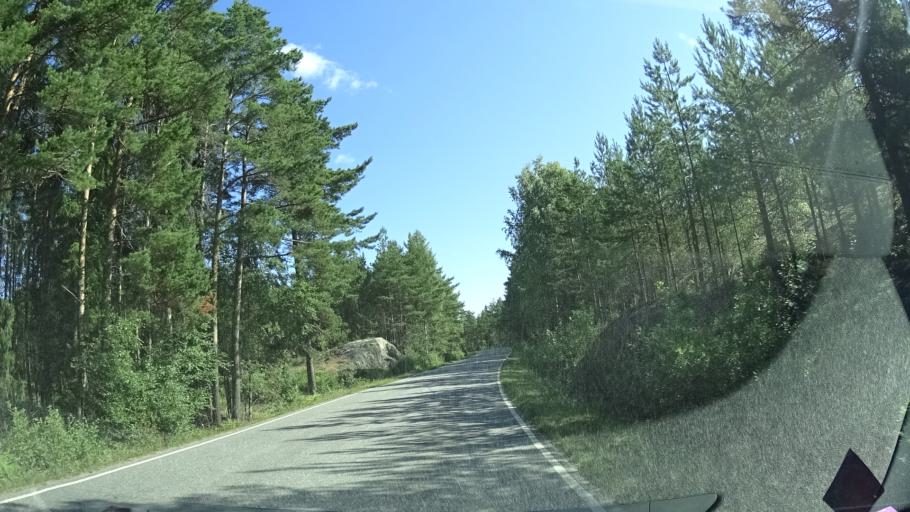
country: FI
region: Varsinais-Suomi
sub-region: Turku
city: Velkua
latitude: 60.4765
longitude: 21.7183
